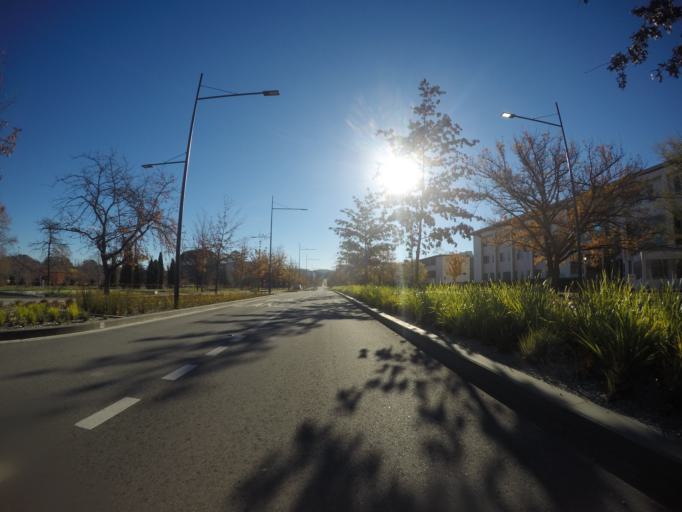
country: AU
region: Australian Capital Territory
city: Canberra
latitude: -35.2873
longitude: 149.1377
